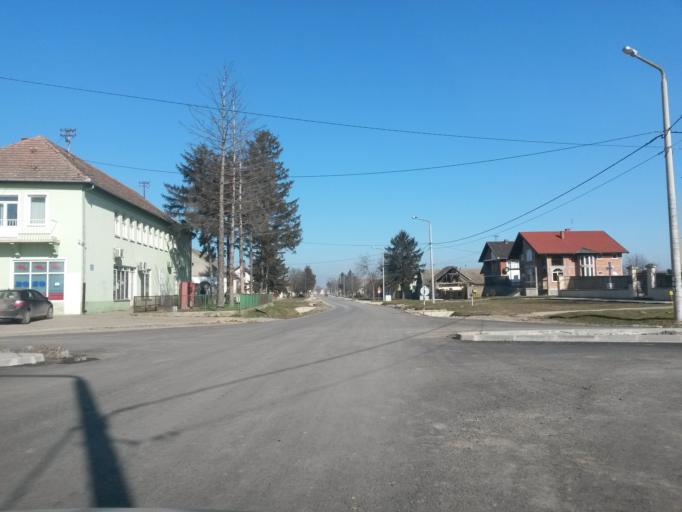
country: HR
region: Vukovarsko-Srijemska
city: Negoslavci
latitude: 45.2782
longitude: 18.9973
